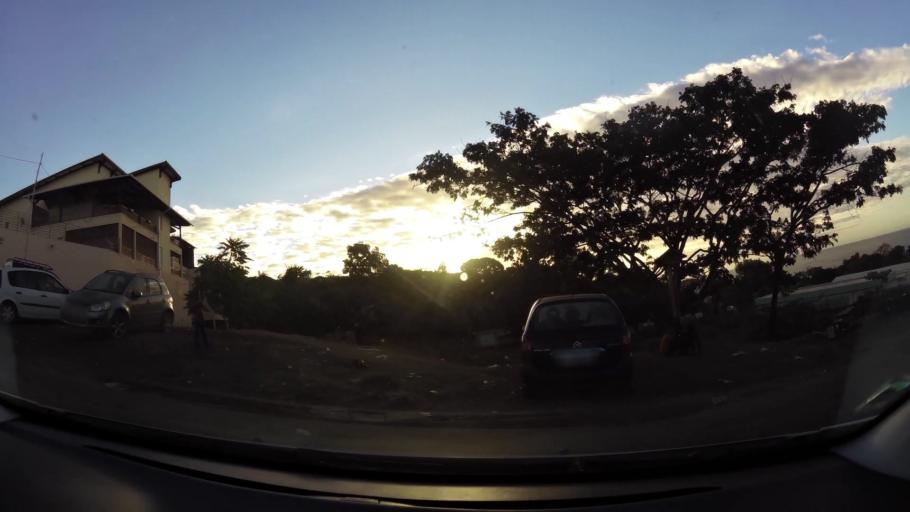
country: YT
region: Koungou
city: Koungou
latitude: -12.7366
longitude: 45.2027
